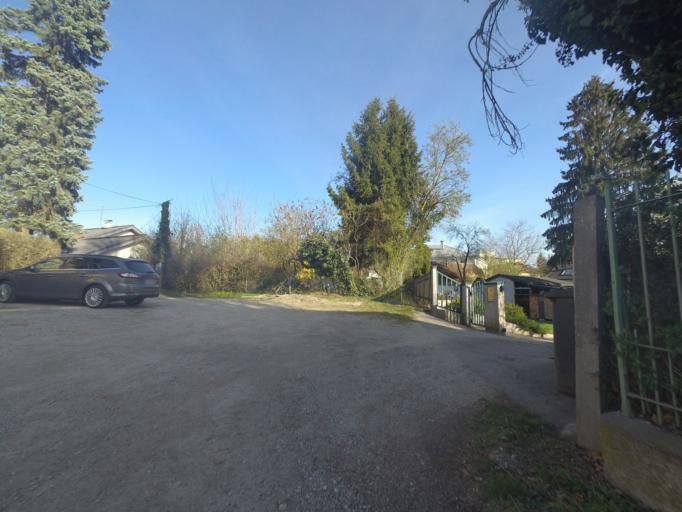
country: AT
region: Salzburg
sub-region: Salzburg Stadt
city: Salzburg
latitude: 47.8018
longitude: 13.0227
